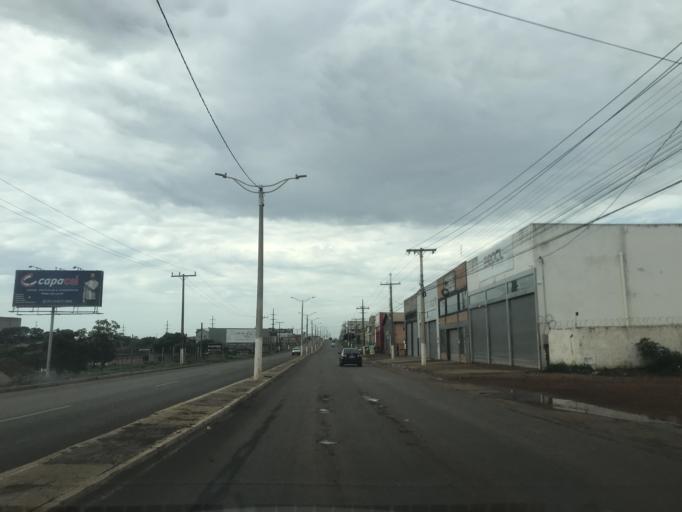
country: BR
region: Goias
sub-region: Luziania
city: Luziania
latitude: -16.2312
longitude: -47.9399
